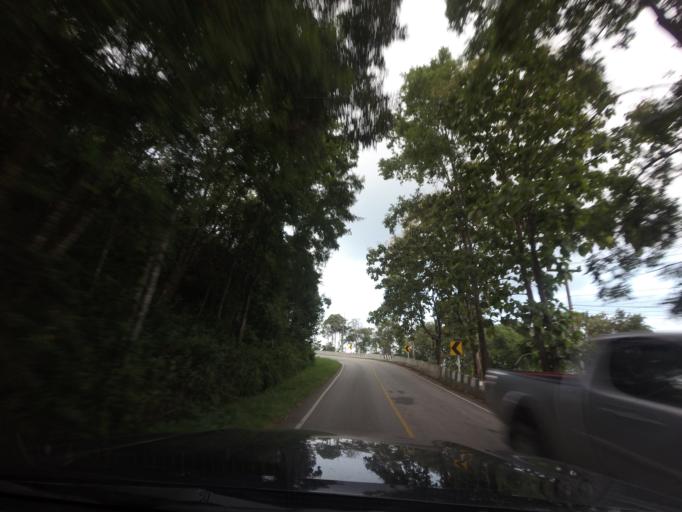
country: TH
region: Loei
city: Dan Sai
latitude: 17.3408
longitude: 101.0821
